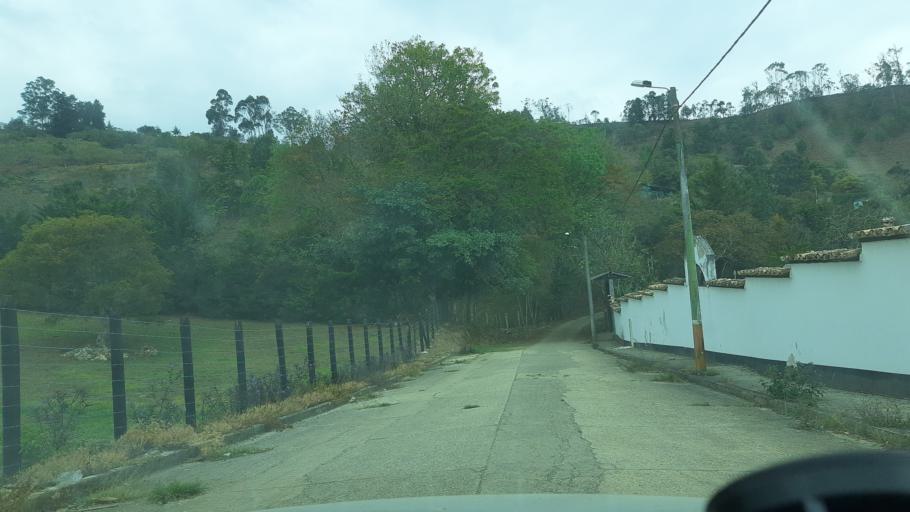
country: CO
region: Boyaca
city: Somondoco
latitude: 4.9722
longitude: -73.3788
